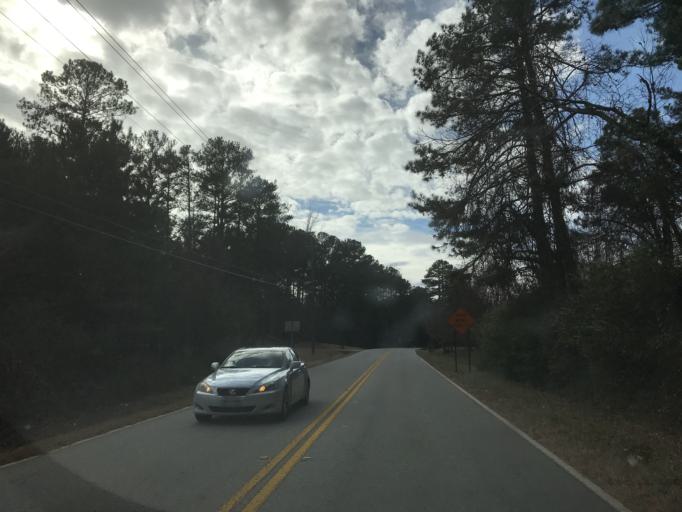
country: US
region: Georgia
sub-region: Douglas County
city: Douglasville
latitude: 33.7844
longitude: -84.7863
